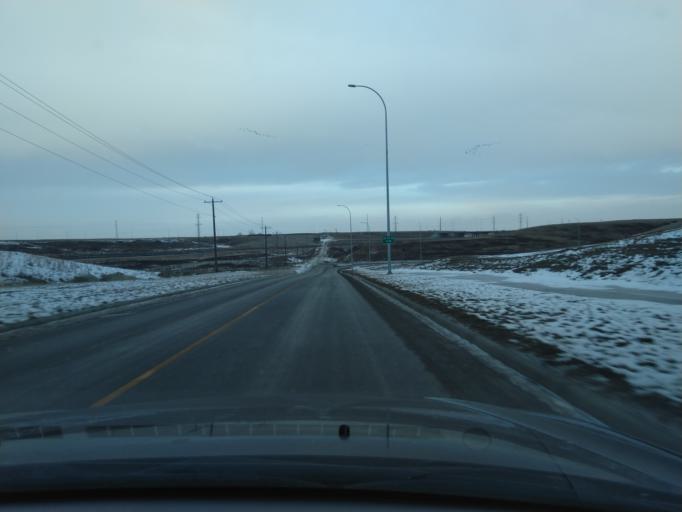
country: CA
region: Alberta
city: Calgary
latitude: 51.1669
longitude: -114.0248
